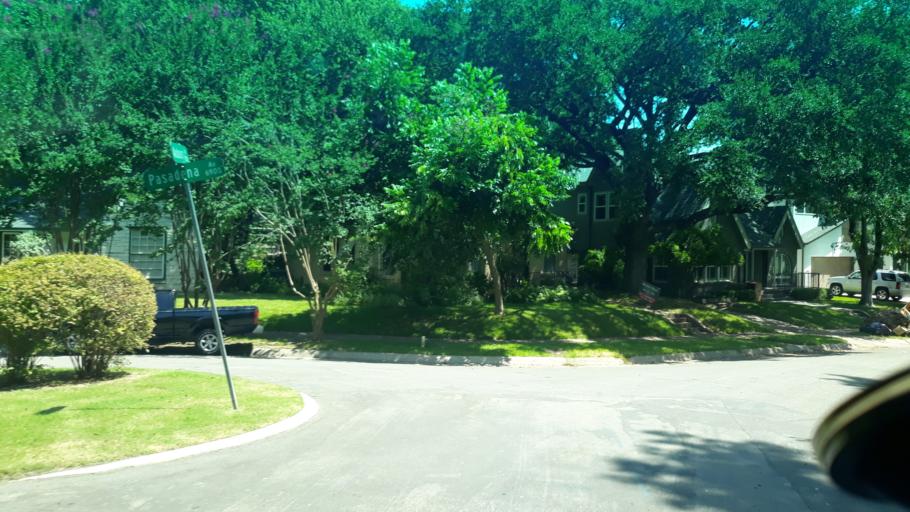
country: US
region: Texas
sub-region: Dallas County
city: Highland Park
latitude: 32.8181
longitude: -96.7393
